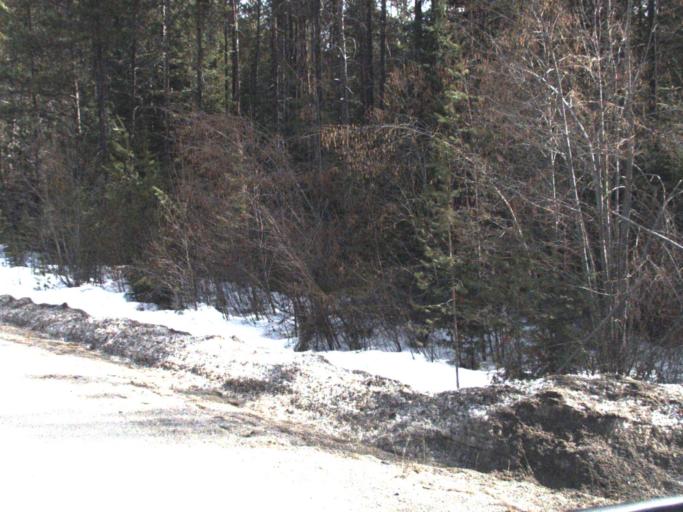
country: US
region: Washington
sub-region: Stevens County
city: Chewelah
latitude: 48.5538
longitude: -117.5621
